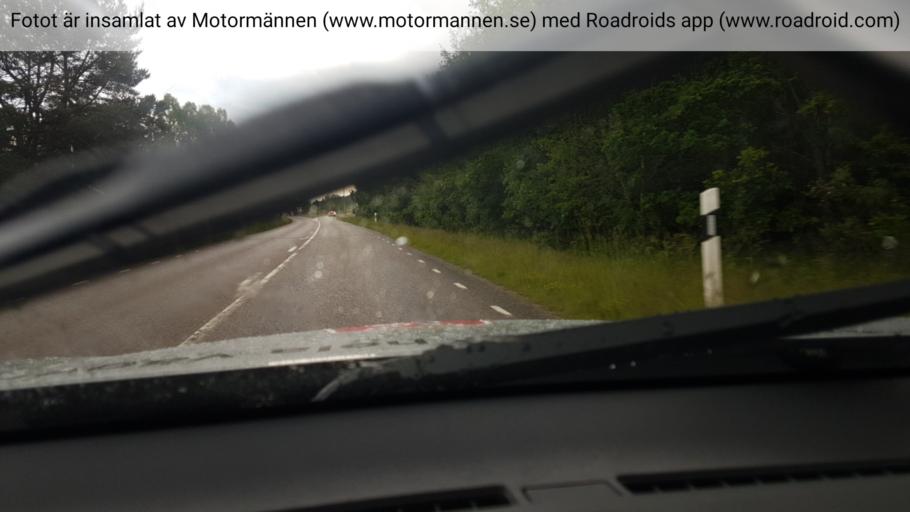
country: SE
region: Vaestra Goetaland
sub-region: Hjo Kommun
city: Hjo
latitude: 58.3063
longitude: 14.2553
